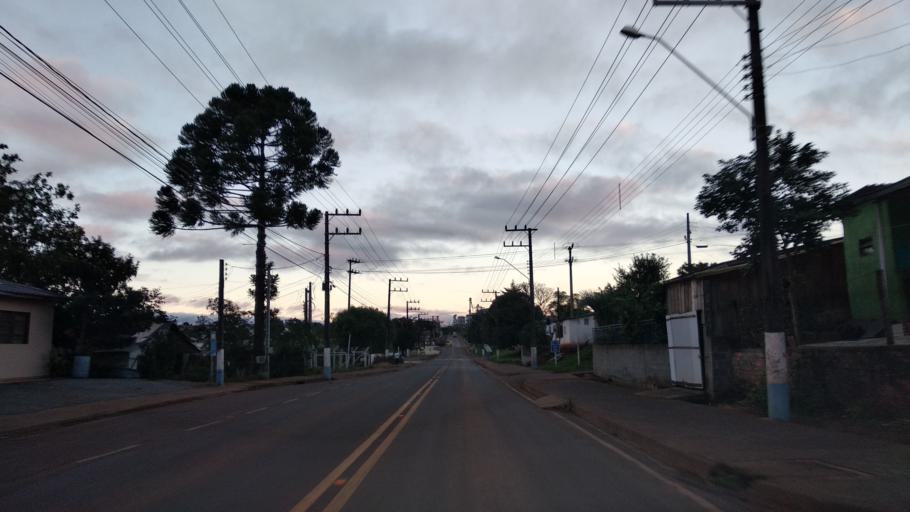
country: BR
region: Santa Catarina
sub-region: Campos Novos
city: Campos Novos
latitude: -27.3837
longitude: -51.2109
